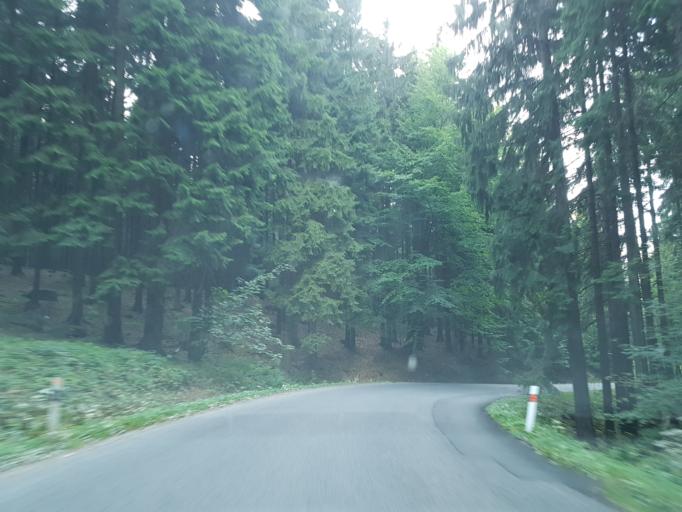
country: CZ
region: Liberecky
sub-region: Okres Jablonec nad Nisou
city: Jablonec nad Nisou
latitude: 50.7138
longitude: 15.1890
